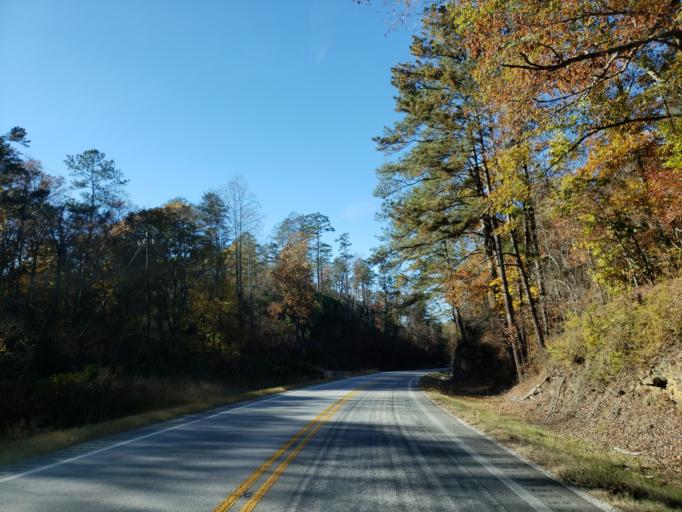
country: US
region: Alabama
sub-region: Calhoun County
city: Choccolocco
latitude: 33.5907
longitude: -85.6889
